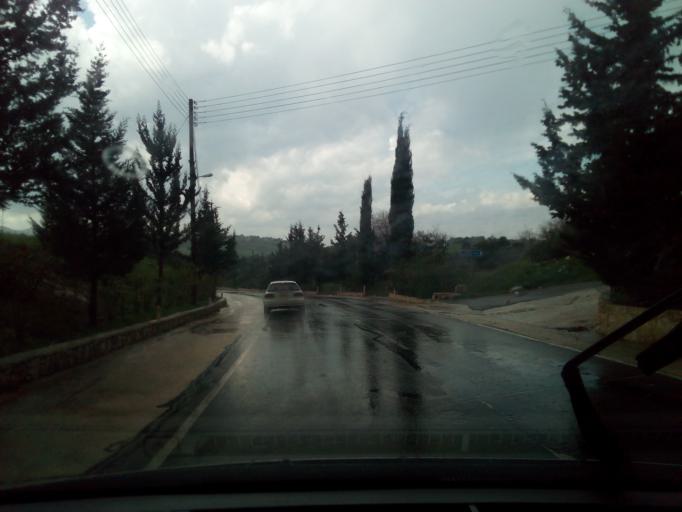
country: CY
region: Pafos
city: Polis
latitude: 35.0019
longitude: 32.4680
